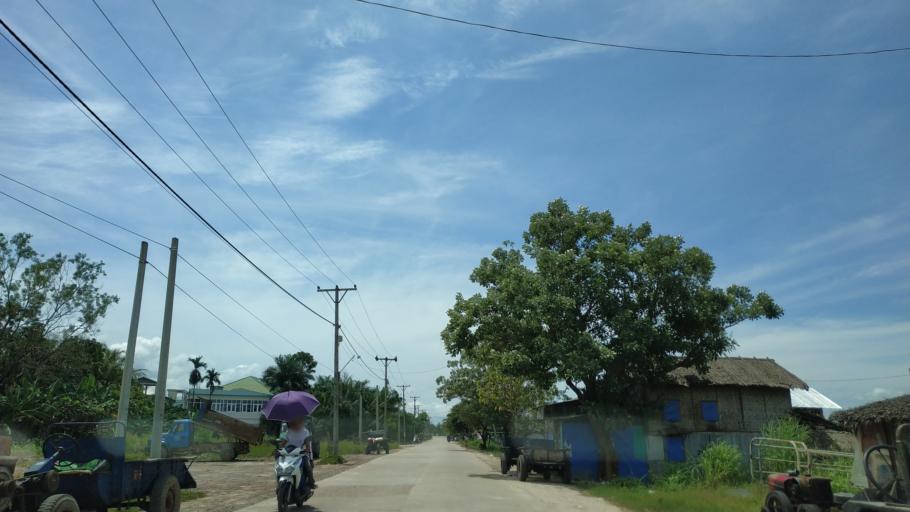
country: MM
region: Tanintharyi
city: Dawei
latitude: 14.0791
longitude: 98.1822
